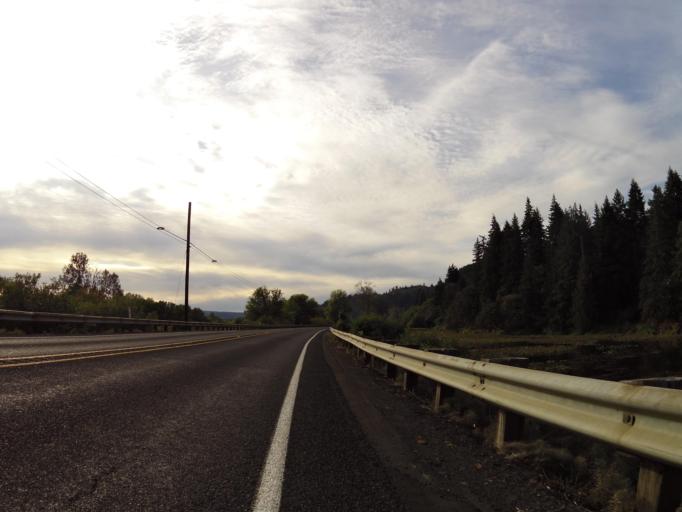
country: US
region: Washington
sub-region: Cowlitz County
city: West Longview
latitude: 46.1832
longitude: -123.0753
